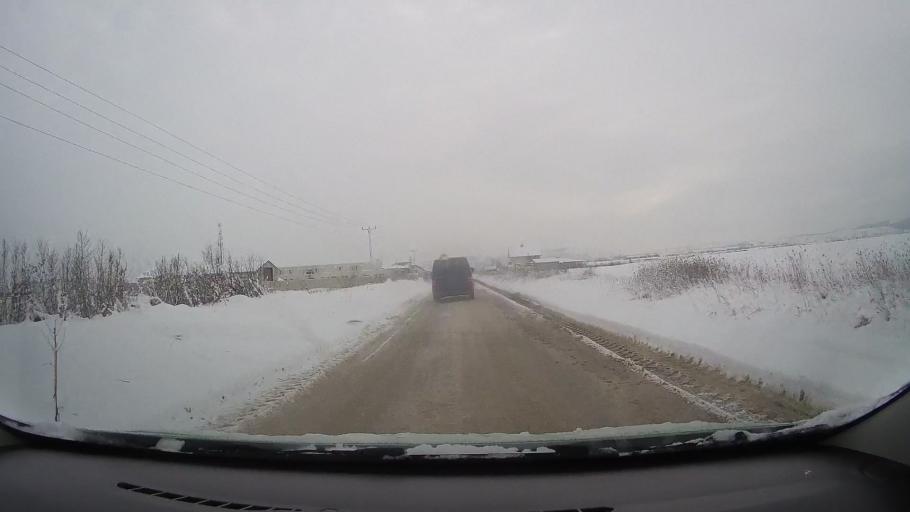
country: RO
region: Alba
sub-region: Municipiul Sebes
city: Lancram
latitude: 45.9601
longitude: 23.5331
